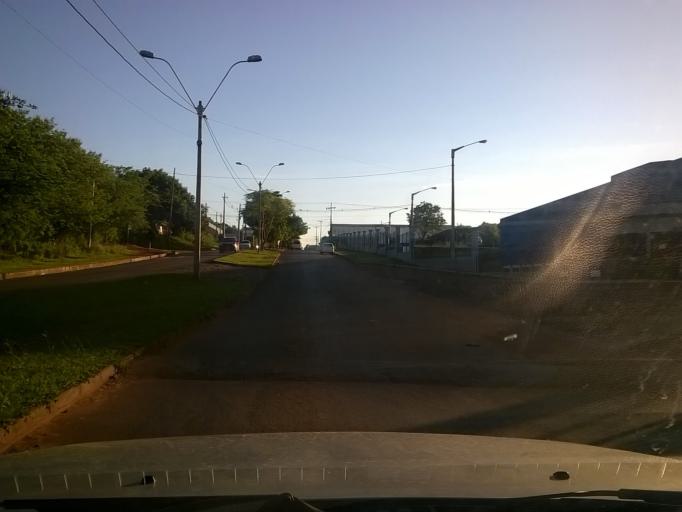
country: PY
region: Alto Parana
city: Presidente Franco
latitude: -25.5321
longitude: -54.6485
